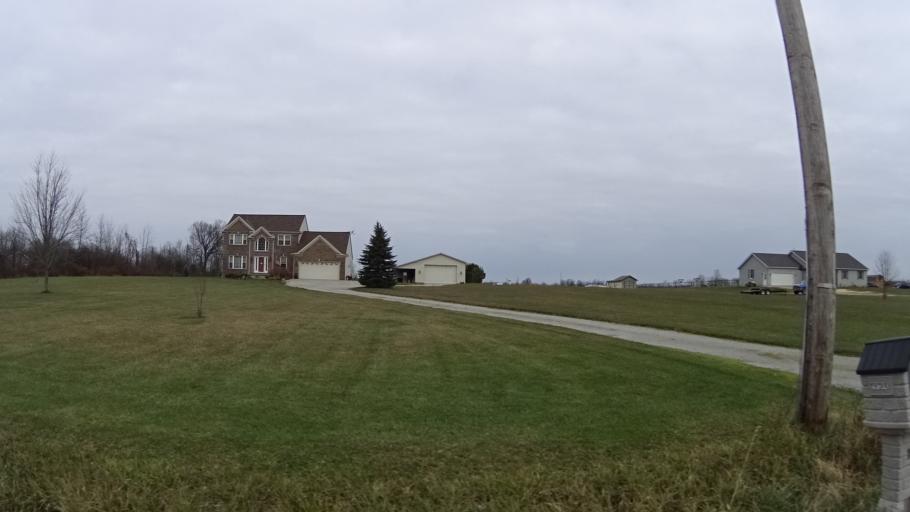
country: US
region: Ohio
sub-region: Lorain County
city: Wellington
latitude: 41.1372
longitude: -82.1768
